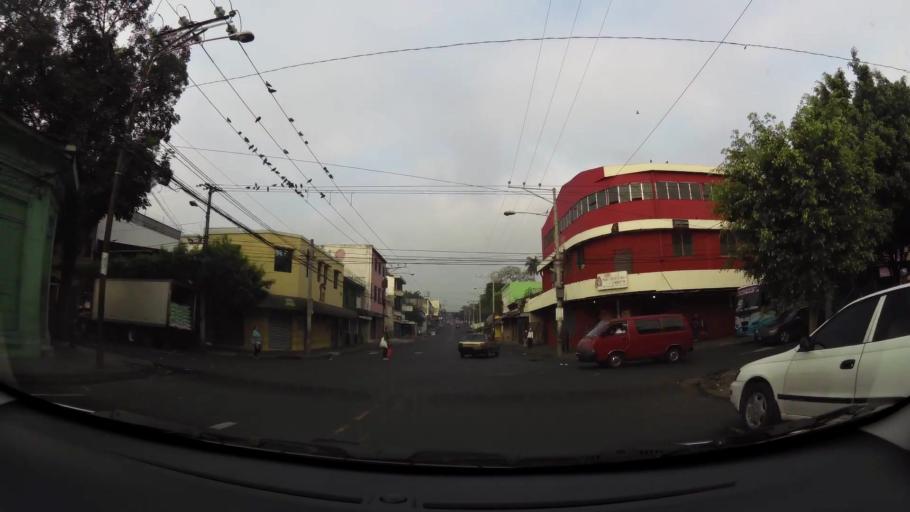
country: SV
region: San Salvador
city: San Salvador
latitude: 13.6978
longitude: -89.1971
